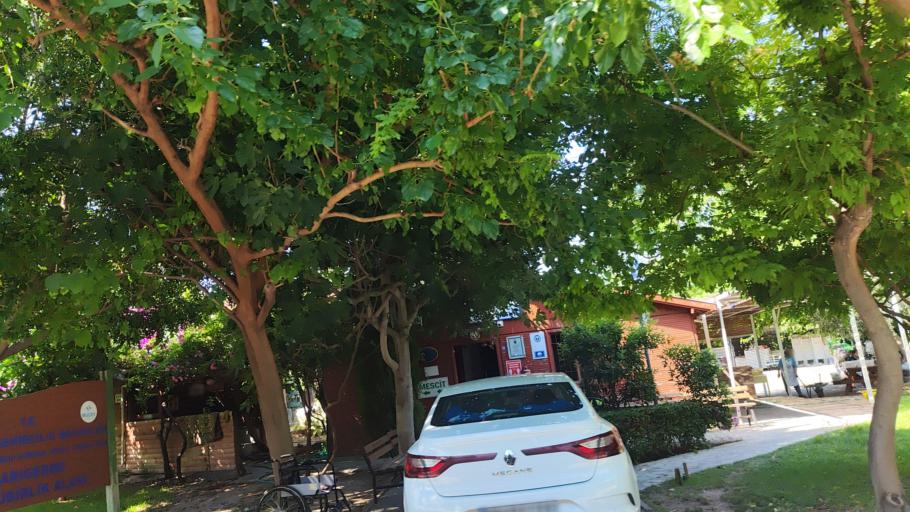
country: TR
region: Mugla
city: Sarigerme
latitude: 36.7019
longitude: 28.6950
